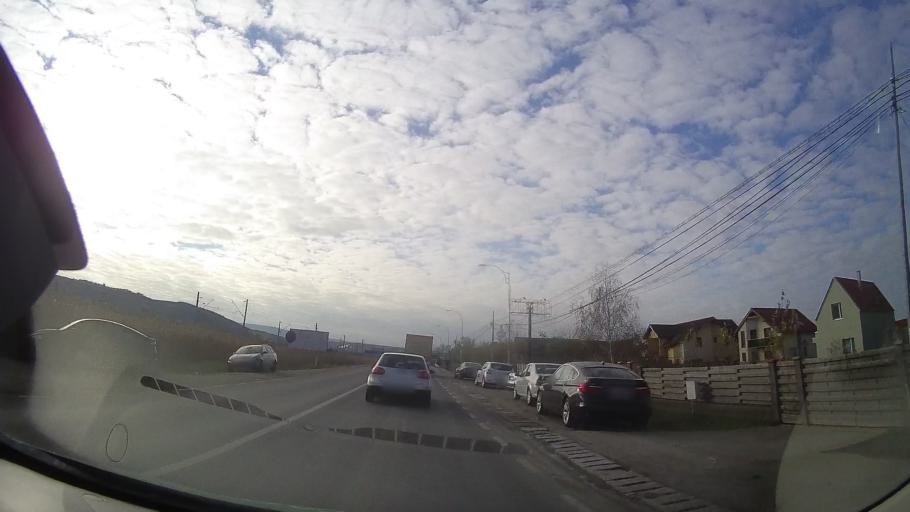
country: RO
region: Cluj
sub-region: Comuna Apahida
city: Sannicoara
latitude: 46.7863
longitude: 23.7275
